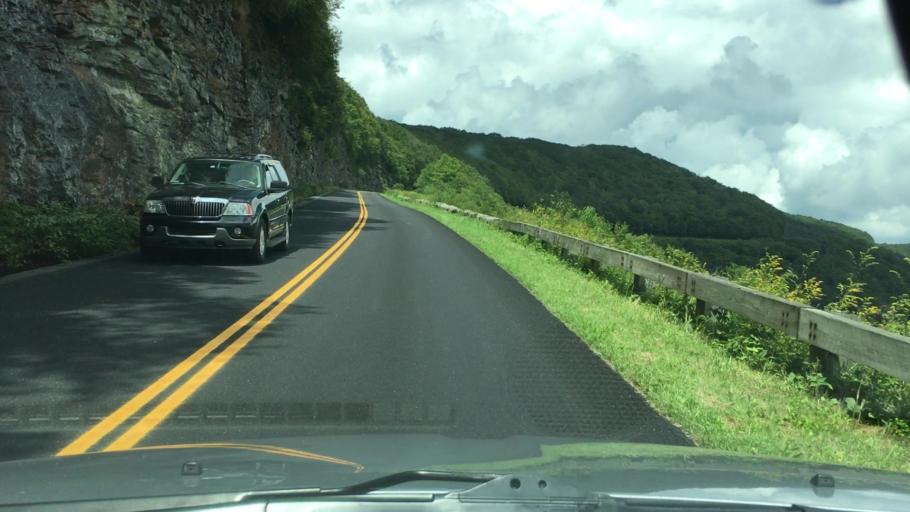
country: US
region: North Carolina
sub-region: Buncombe County
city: Swannanoa
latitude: 35.6900
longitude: -82.3837
